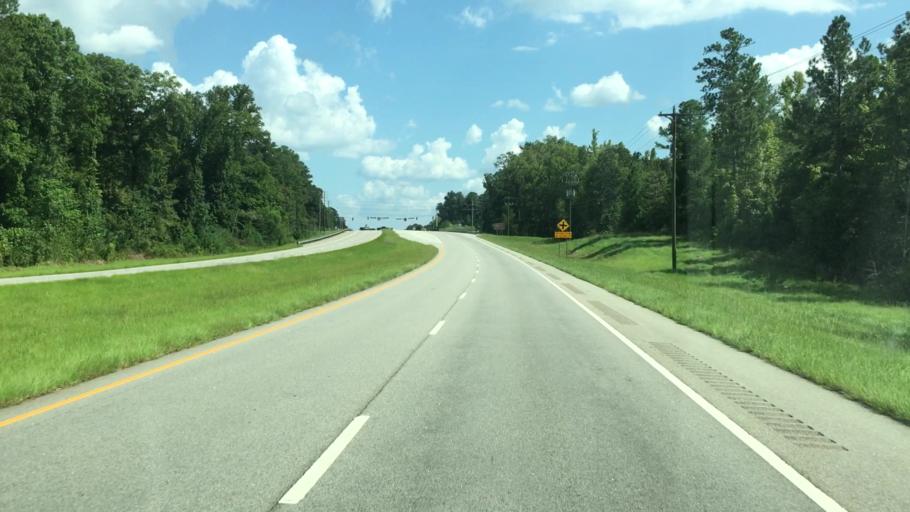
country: US
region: Georgia
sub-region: Putnam County
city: Eatonton
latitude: 33.2403
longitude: -83.3217
